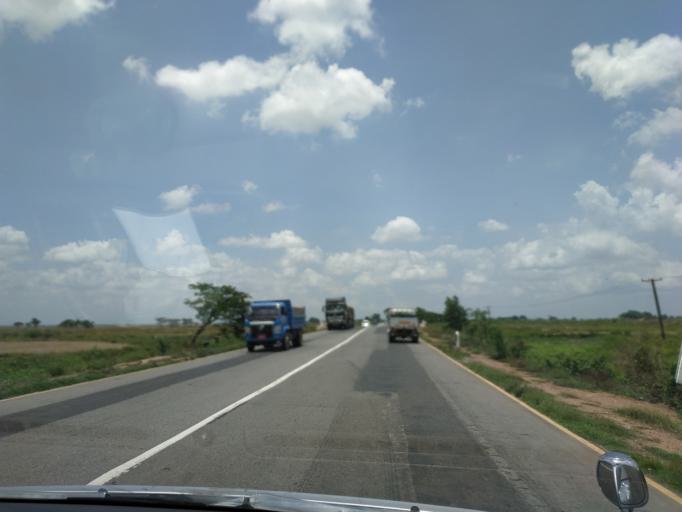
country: MM
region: Bago
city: Bago
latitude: 17.4633
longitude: 96.5916
